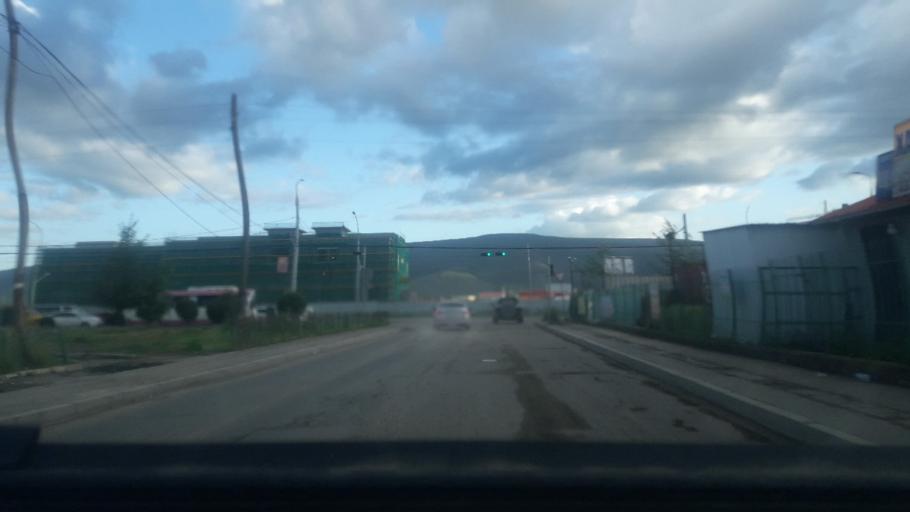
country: MN
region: Ulaanbaatar
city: Ulaanbaatar
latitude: 47.9136
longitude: 106.9946
